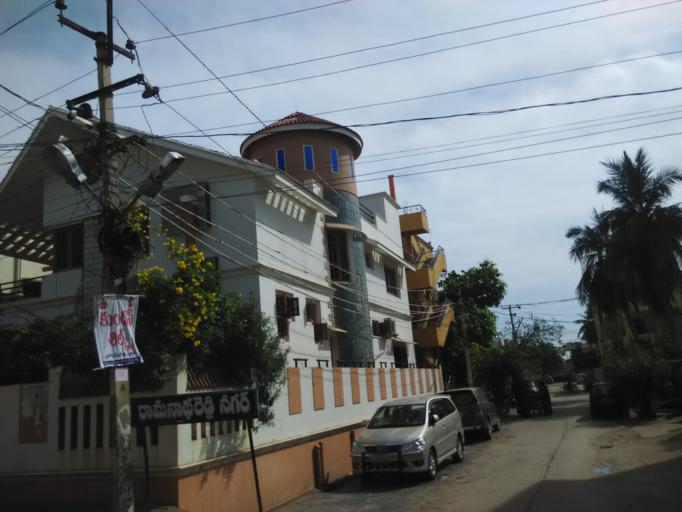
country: IN
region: Andhra Pradesh
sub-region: Kurnool
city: Nandyal
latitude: 15.4846
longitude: 78.4802
